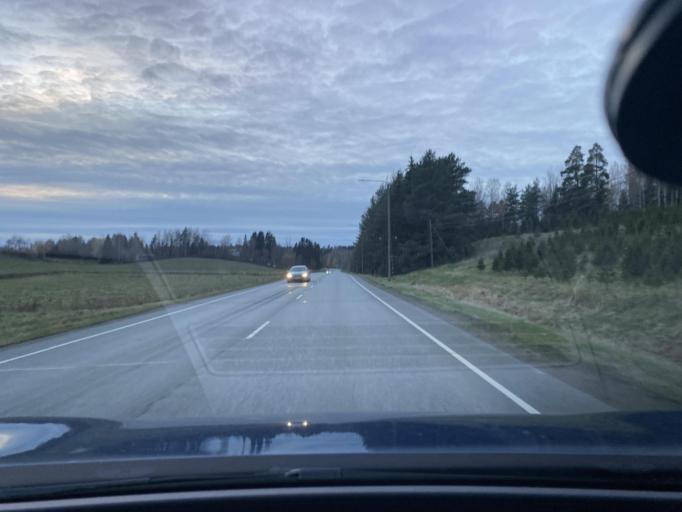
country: FI
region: Uusimaa
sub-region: Helsinki
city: Saukkola
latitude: 60.3887
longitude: 24.0414
